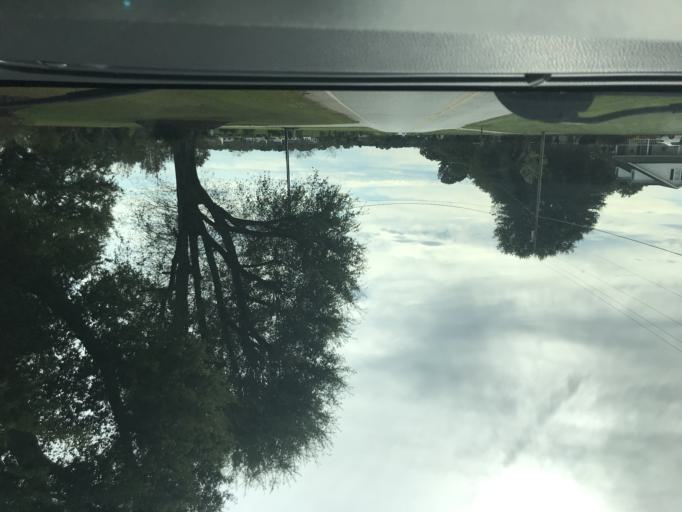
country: US
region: South Carolina
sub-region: Cherokee County
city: Gaffney
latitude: 35.1370
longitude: -81.6795
